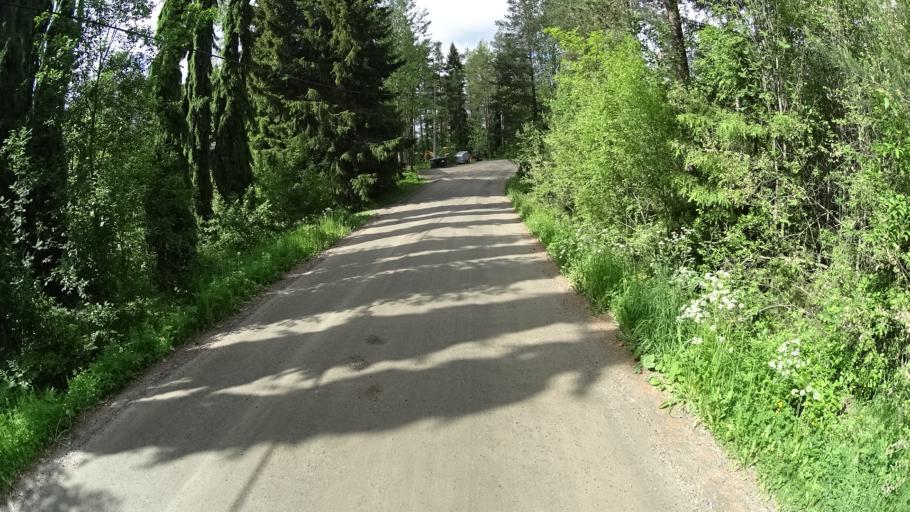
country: FI
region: Uusimaa
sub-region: Helsinki
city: Sibbo
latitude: 60.2811
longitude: 25.3148
